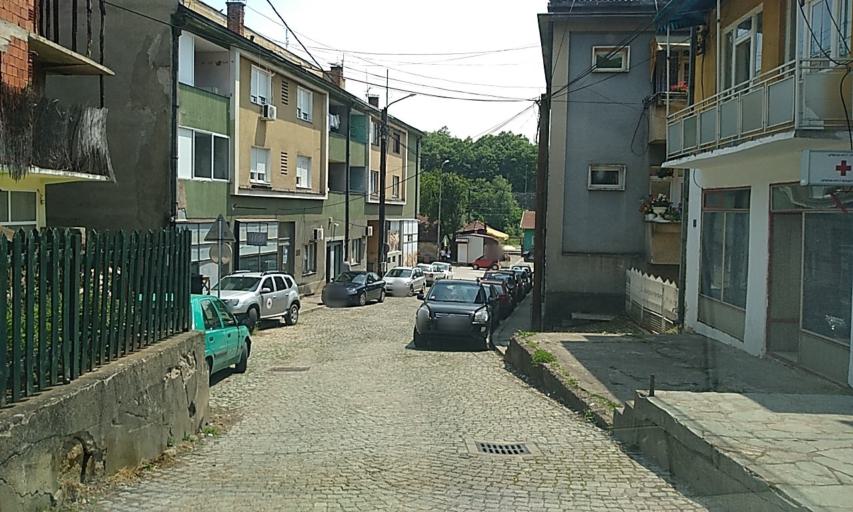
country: RS
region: Central Serbia
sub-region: Pcinjski Okrug
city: Vladicin Han
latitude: 42.7104
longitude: 22.0604
